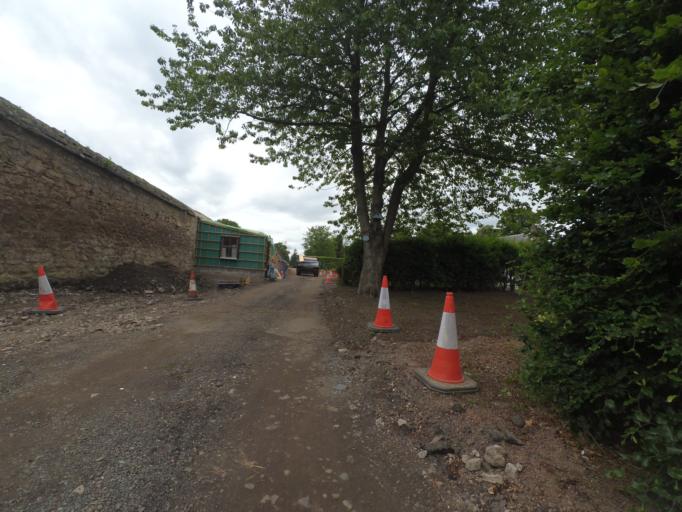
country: GB
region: Scotland
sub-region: East Lothian
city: Pencaitland
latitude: 55.9164
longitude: -2.8986
